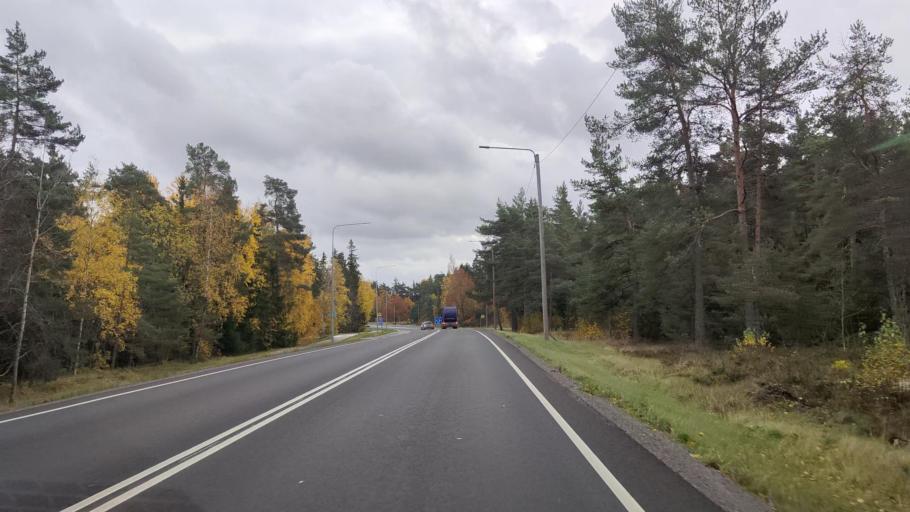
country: FI
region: Varsinais-Suomi
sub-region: Turku
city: Kaarina
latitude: 60.4495
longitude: 22.3730
